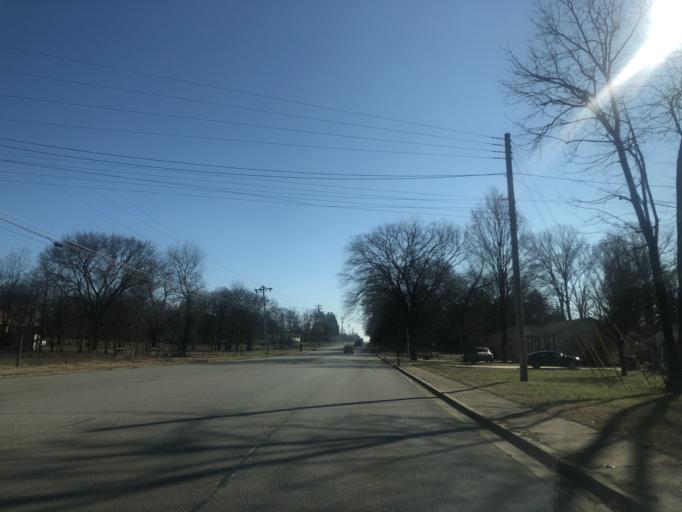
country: US
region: Tennessee
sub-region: Rutherford County
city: Smyrna
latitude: 35.9428
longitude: -86.5023
